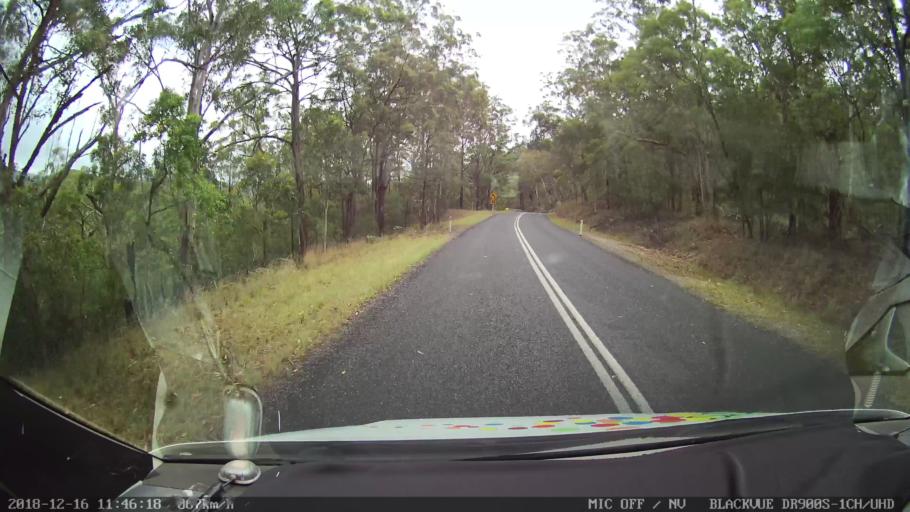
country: AU
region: New South Wales
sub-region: Tenterfield Municipality
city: Carrolls Creek
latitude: -28.9292
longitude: 152.2301
